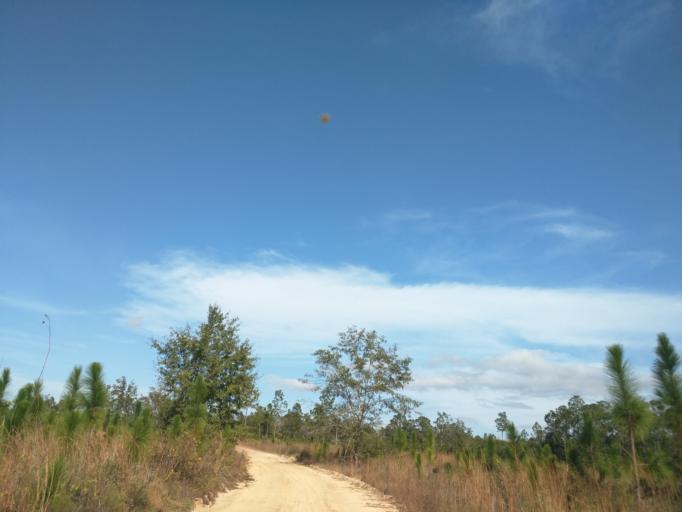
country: US
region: Florida
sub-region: Escambia County
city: Cantonment
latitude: 30.5479
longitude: -87.4300
